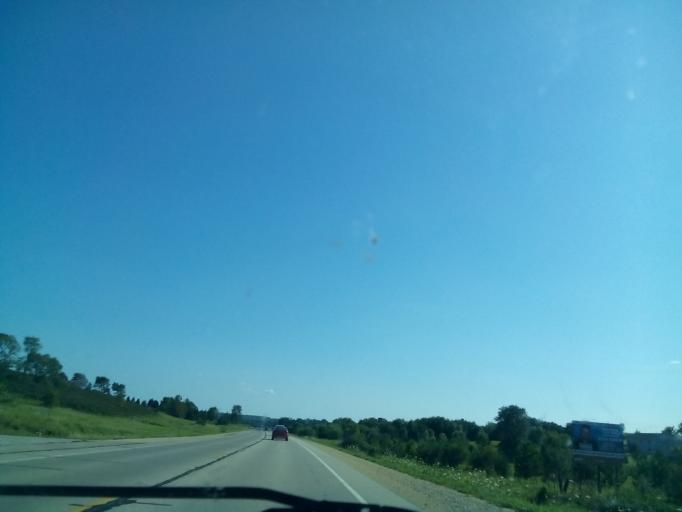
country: US
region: Wisconsin
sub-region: Green County
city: New Glarus
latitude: 42.8368
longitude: -89.6350
